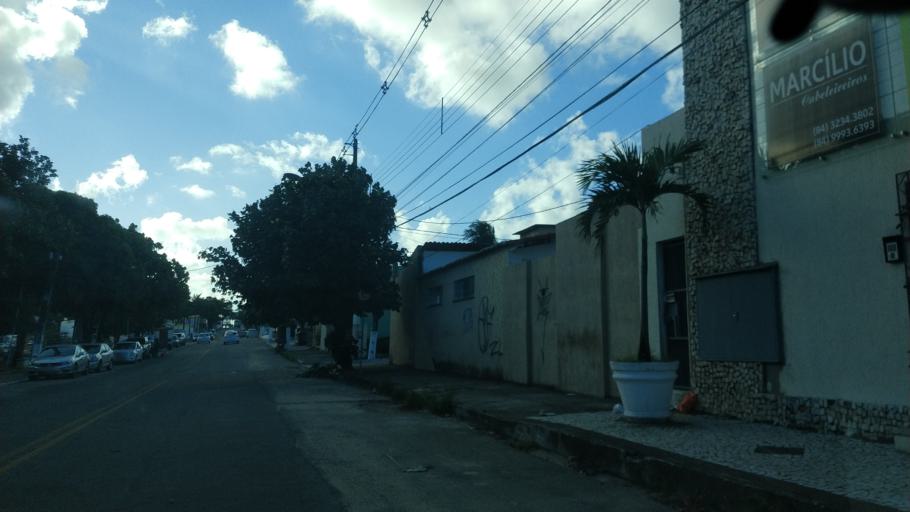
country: BR
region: Rio Grande do Norte
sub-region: Natal
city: Natal
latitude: -5.8449
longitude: -35.2080
